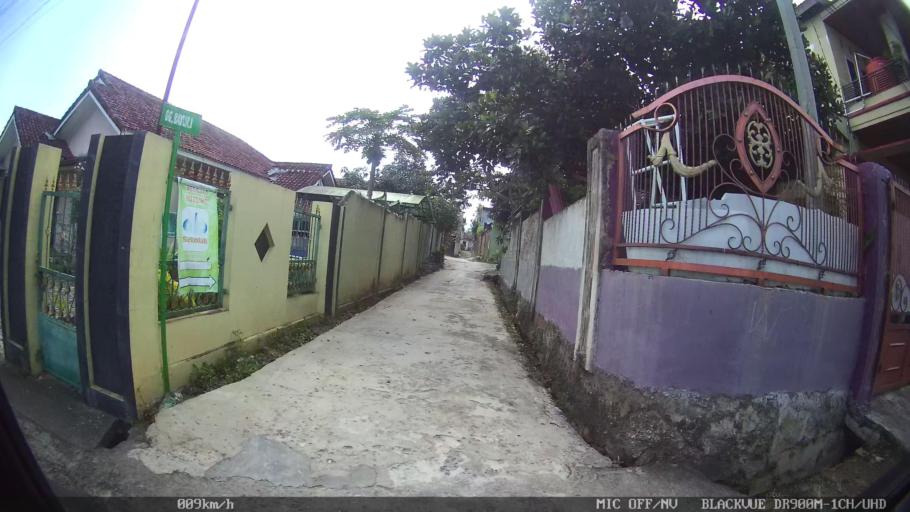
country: ID
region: Lampung
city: Kedaton
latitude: -5.3905
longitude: 105.2084
